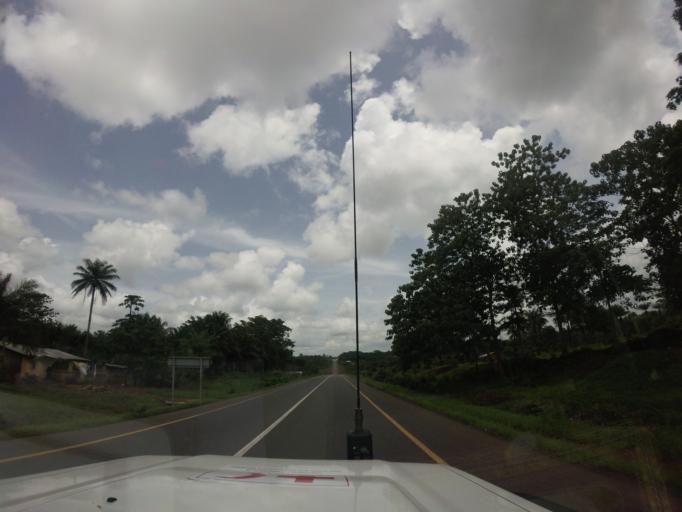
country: SL
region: Northern Province
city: Kambia
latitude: 9.0736
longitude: -12.9143
